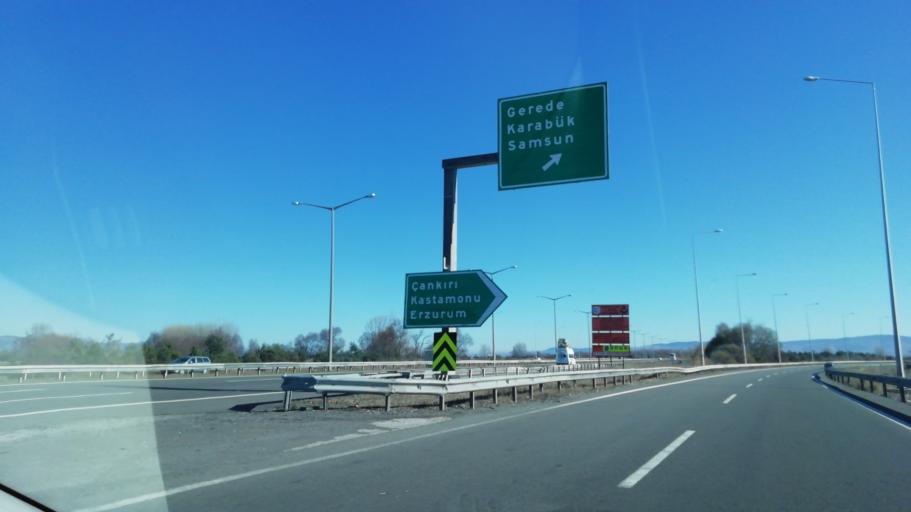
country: TR
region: Bolu
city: Gerede
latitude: 40.7394
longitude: 32.1801
